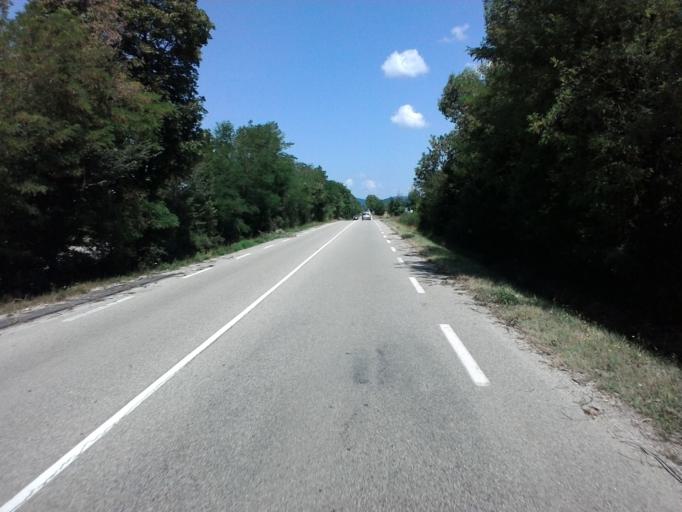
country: FR
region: Rhone-Alpes
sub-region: Departement de l'Ain
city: Ambronay
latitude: 46.0160
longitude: 5.3401
